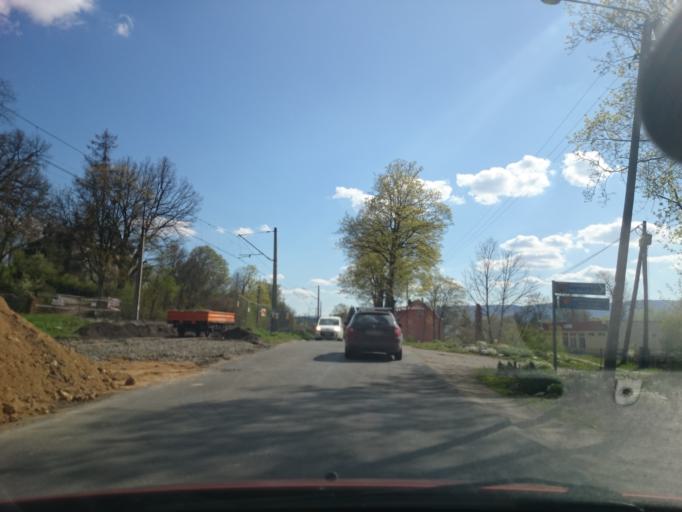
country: PL
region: Lower Silesian Voivodeship
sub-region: Powiat klodzki
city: Klodzko
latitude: 50.3905
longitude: 16.6351
